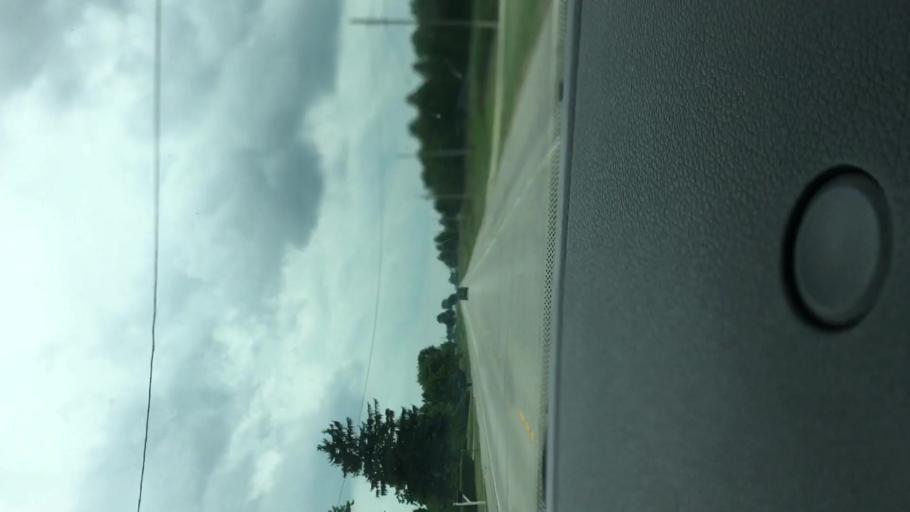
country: US
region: Indiana
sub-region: Randolph County
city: Winchester
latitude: 40.2642
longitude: -84.9763
